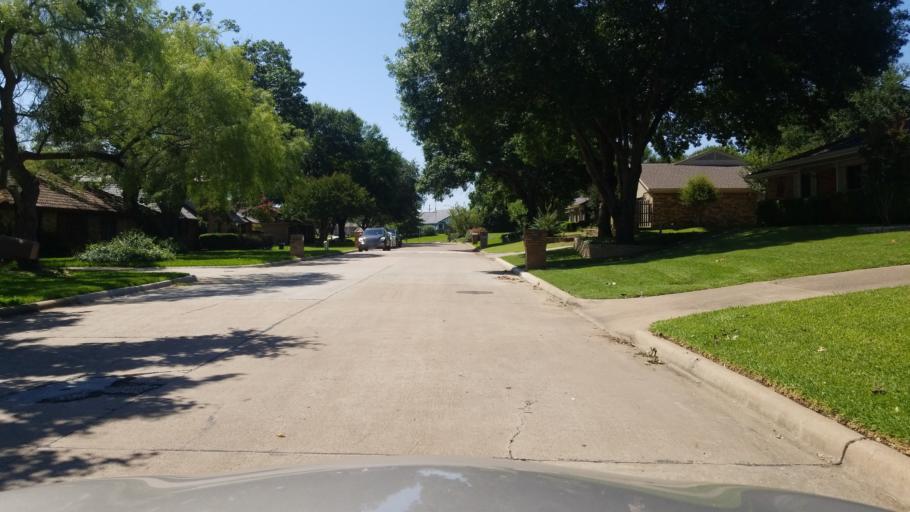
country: US
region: Texas
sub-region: Dallas County
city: Grand Prairie
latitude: 32.6905
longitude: -97.0010
